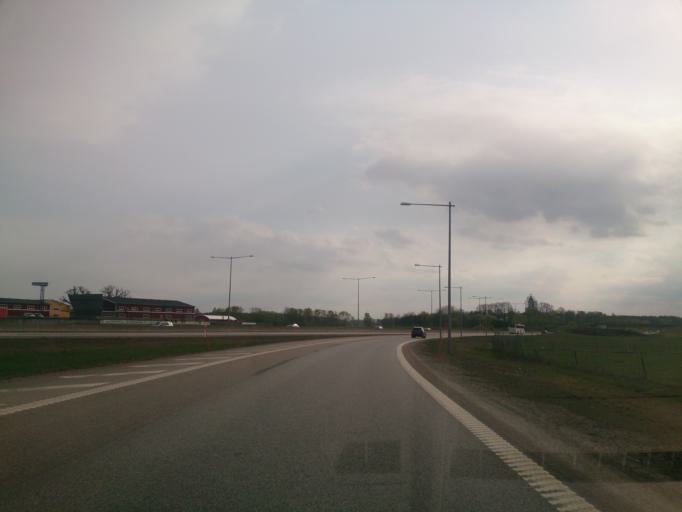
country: SE
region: OEstergoetland
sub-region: Norrkopings Kommun
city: Norrkoping
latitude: 58.5786
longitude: 16.1049
